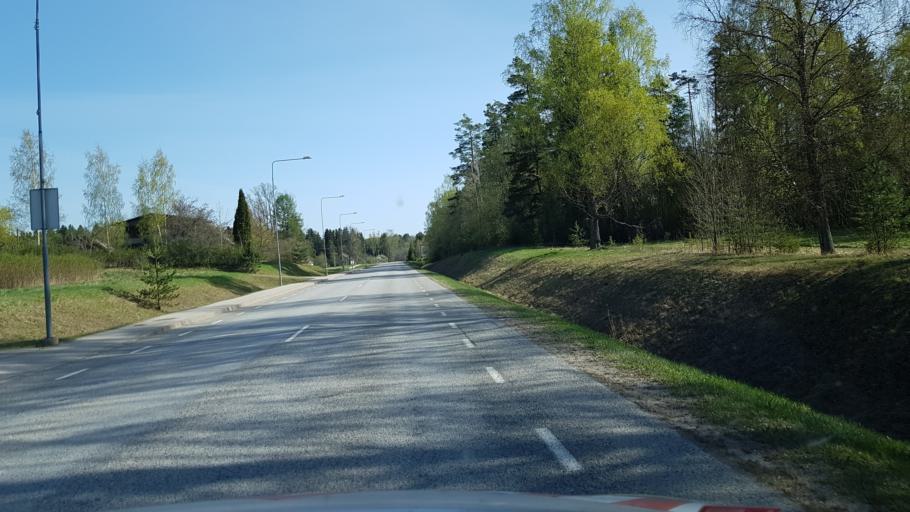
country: EE
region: Viljandimaa
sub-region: Abja vald
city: Abja-Paluoja
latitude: 58.1328
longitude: 25.3657
